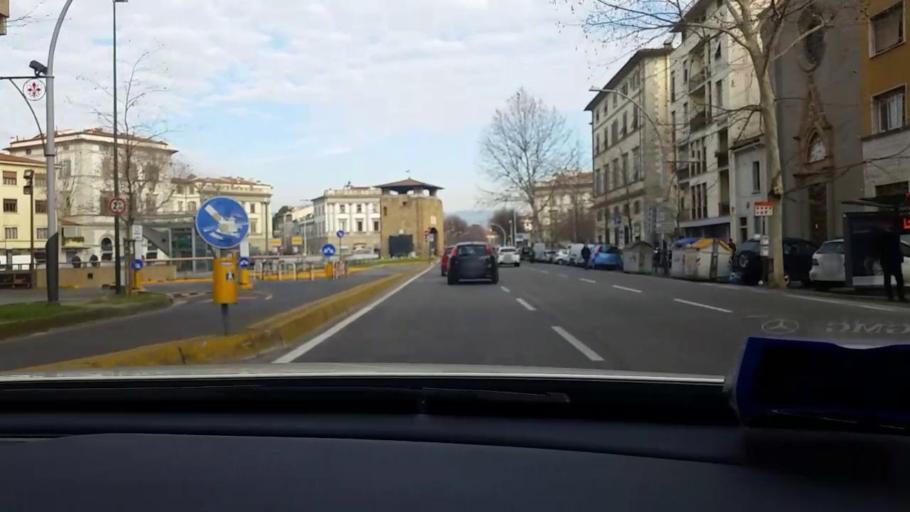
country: IT
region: Tuscany
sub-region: Province of Florence
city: Florence
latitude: 43.7693
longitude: 11.2711
